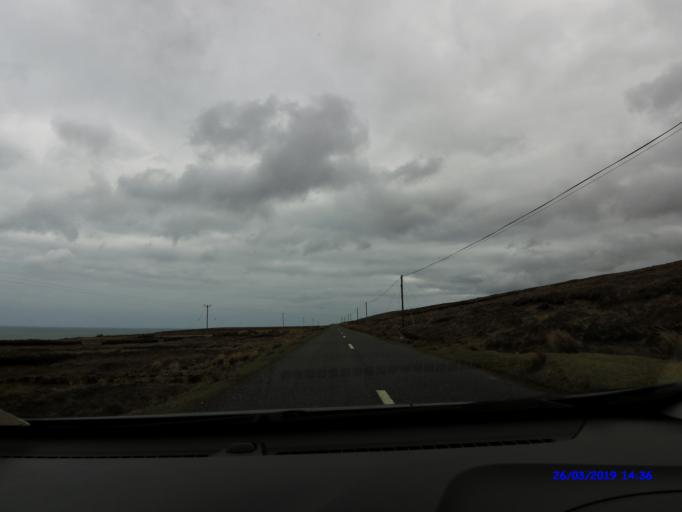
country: IE
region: Connaught
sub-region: Maigh Eo
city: Crossmolina
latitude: 54.3057
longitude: -9.5258
